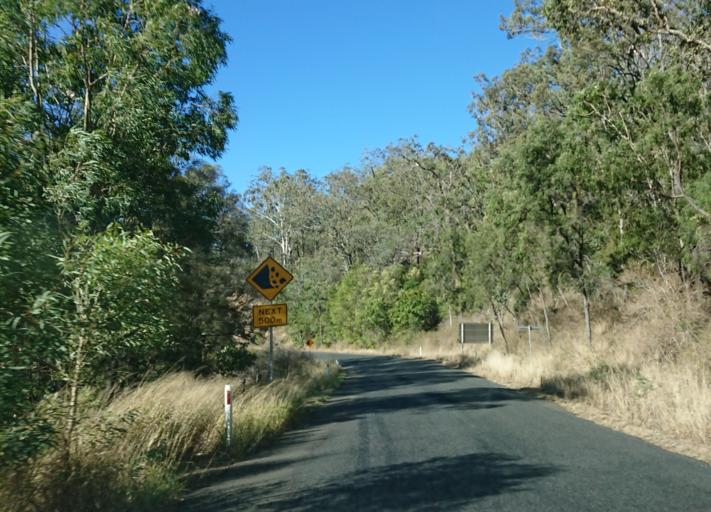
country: AU
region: Queensland
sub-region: Toowoomba
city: Top Camp
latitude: -27.7502
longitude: 152.0841
